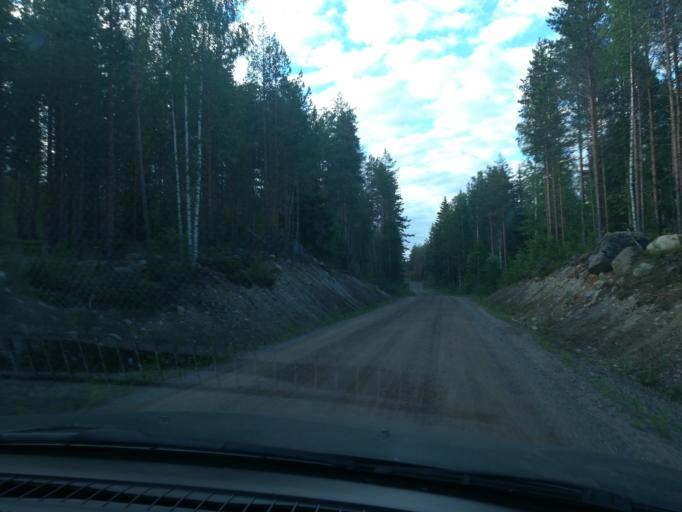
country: FI
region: Southern Savonia
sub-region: Mikkeli
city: Puumala
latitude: 61.5791
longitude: 28.1630
